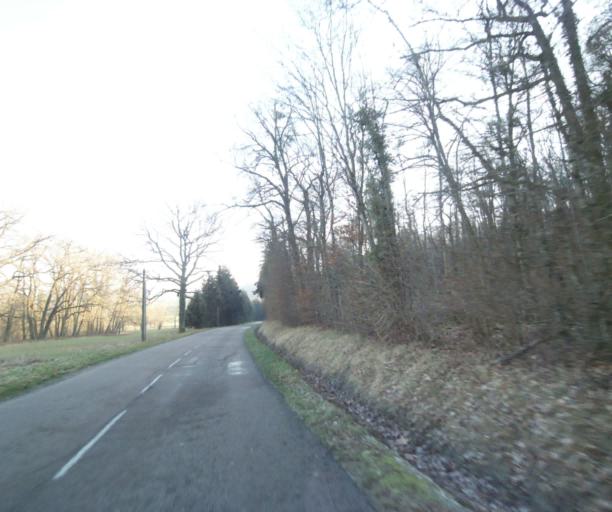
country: FR
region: Champagne-Ardenne
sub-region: Departement de la Haute-Marne
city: Bienville
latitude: 48.5587
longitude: 5.0851
